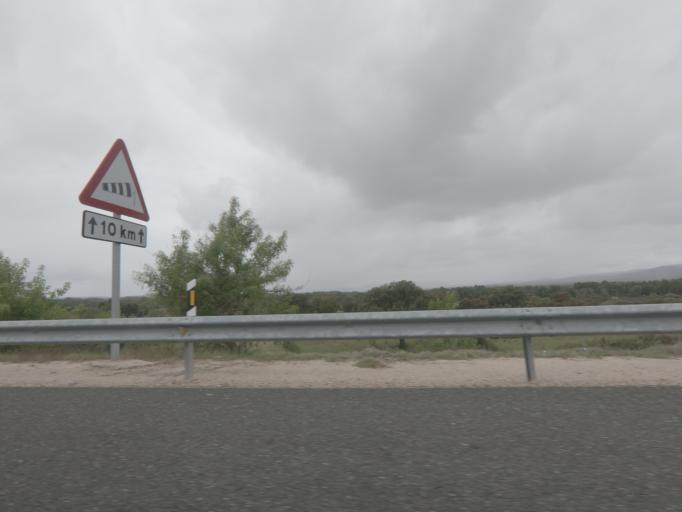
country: ES
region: Extremadura
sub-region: Provincia de Caceres
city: Casas del Monte
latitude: 40.2192
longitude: -5.9854
